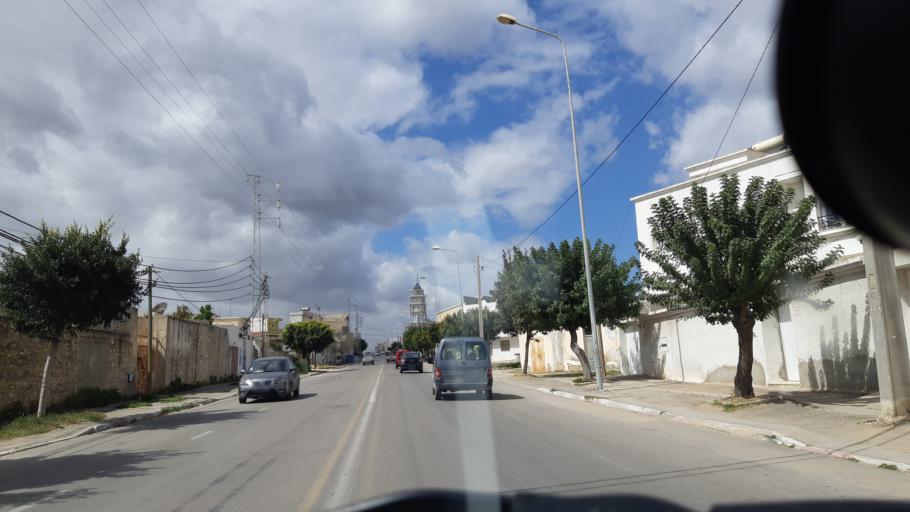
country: TN
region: Susah
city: Akouda
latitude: 35.8776
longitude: 10.5314
